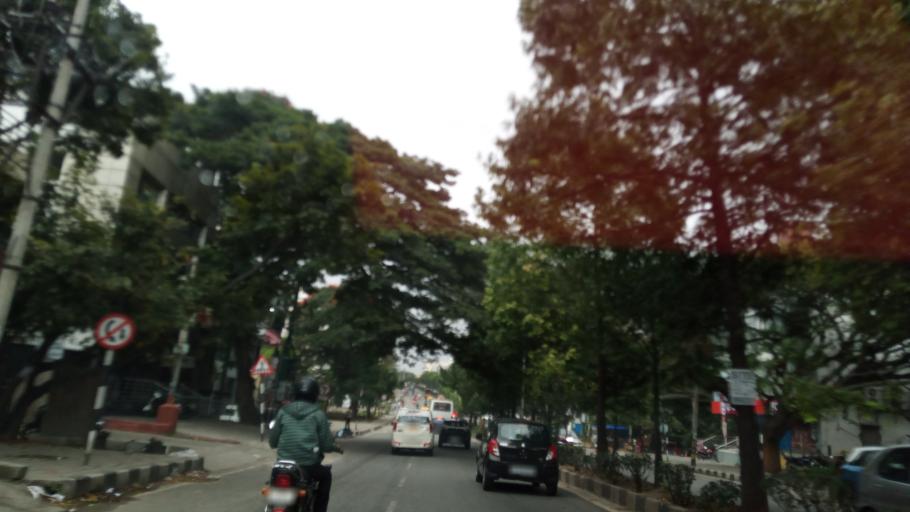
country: IN
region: Karnataka
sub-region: Bangalore Urban
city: Bangalore
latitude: 12.9271
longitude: 77.5475
